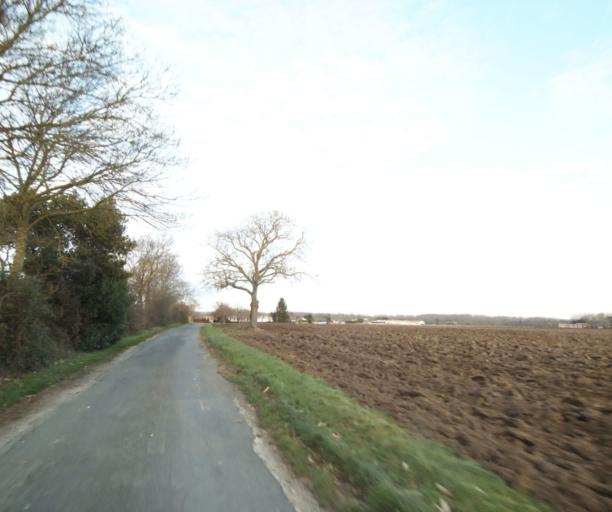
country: FR
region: Poitou-Charentes
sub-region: Departement de la Charente-Maritime
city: Les Gonds
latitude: 45.7083
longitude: -0.6124
